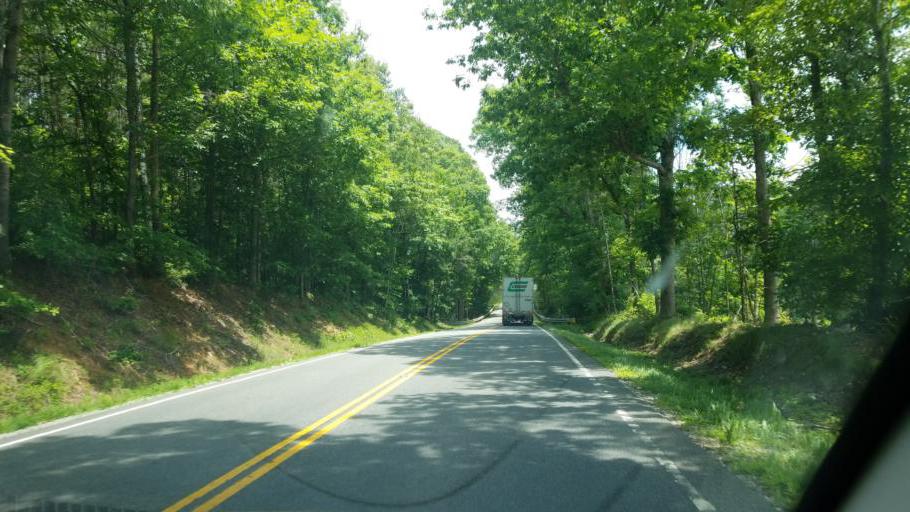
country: US
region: Virginia
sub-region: Amherst County
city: Amherst
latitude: 37.5674
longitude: -78.9243
